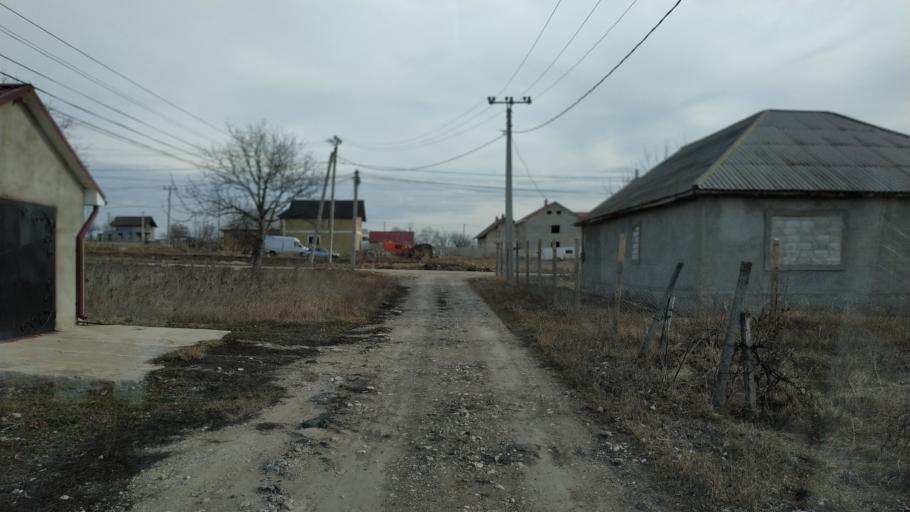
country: MD
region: Chisinau
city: Vatra
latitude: 46.9890
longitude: 28.6686
